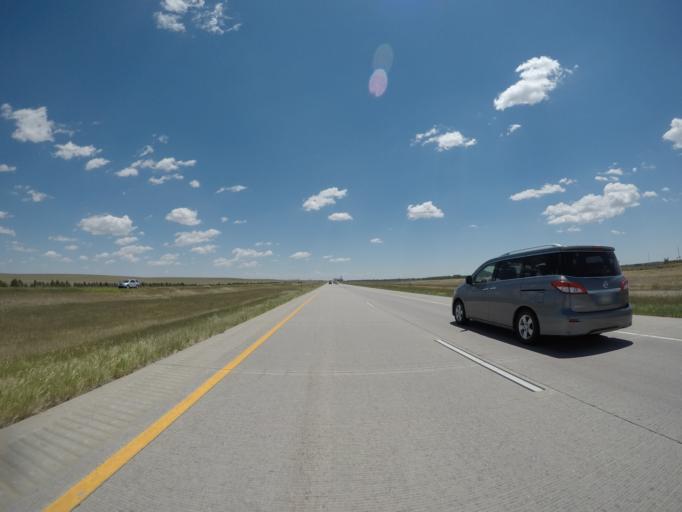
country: US
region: Colorado
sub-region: Lincoln County
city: Limon
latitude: 39.2762
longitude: -103.7489
